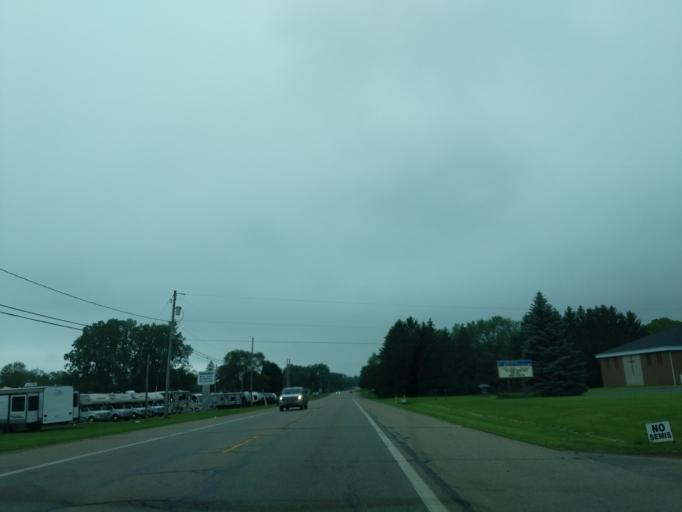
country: US
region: Michigan
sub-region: Branch County
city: Quincy
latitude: 41.9394
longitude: -84.9273
